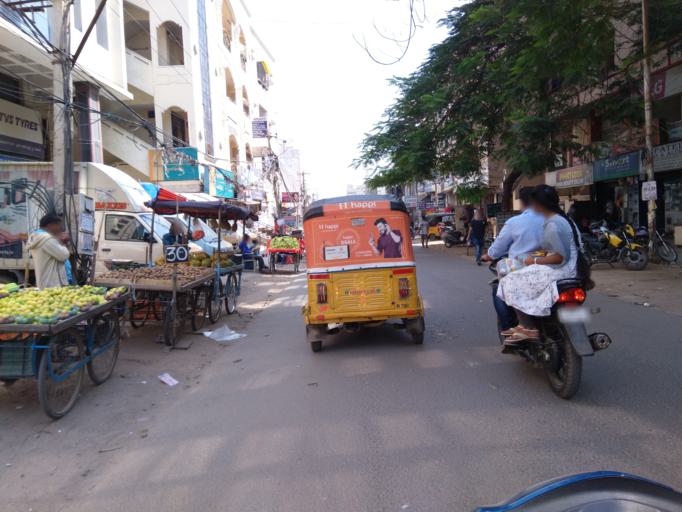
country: IN
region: Telangana
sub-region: Rangareddi
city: Kukatpalli
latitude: 17.4961
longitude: 78.4050
